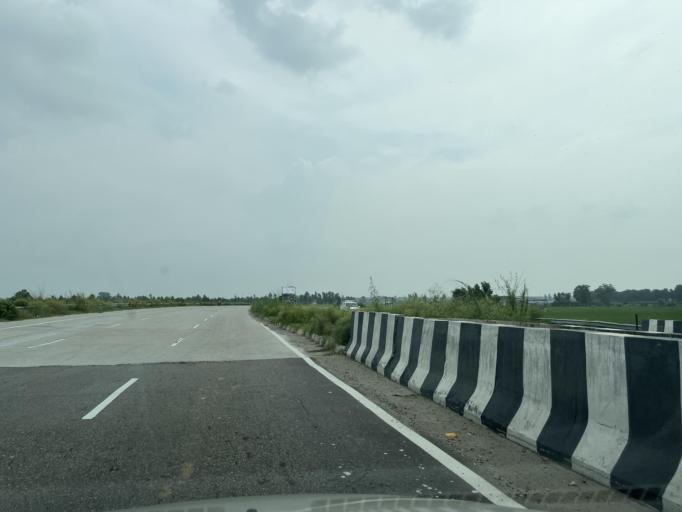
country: IN
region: Uttarakhand
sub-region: Udham Singh Nagar
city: Kashipur
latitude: 29.1895
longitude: 78.9391
